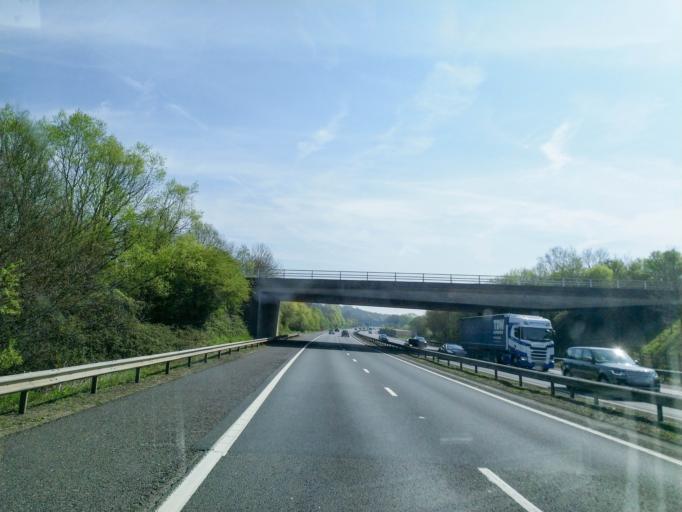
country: GB
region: England
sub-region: Kent
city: Shoreham
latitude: 51.3044
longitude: 0.1899
